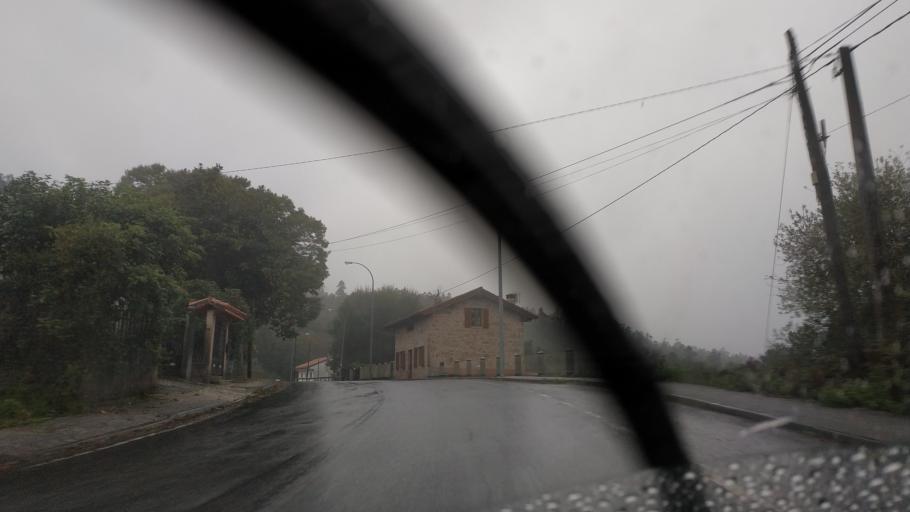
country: ES
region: Galicia
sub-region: Provincia da Coruna
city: Negreira
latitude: 42.9064
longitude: -8.7434
